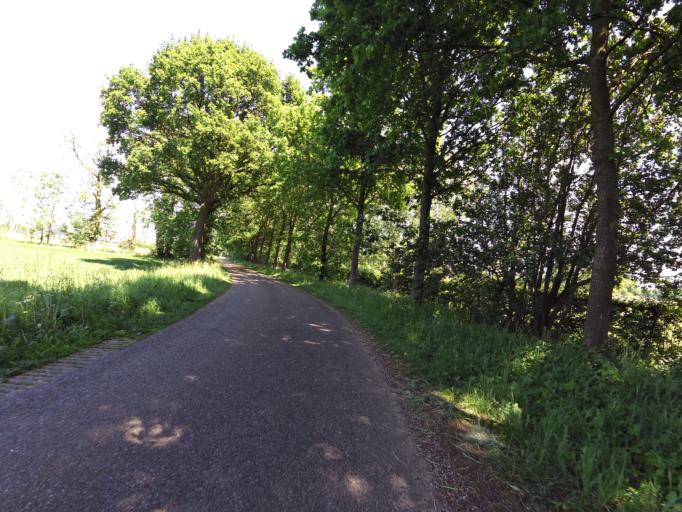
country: NL
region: Gelderland
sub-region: Gemeente Bronckhorst
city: Hengelo
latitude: 52.0618
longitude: 6.2777
